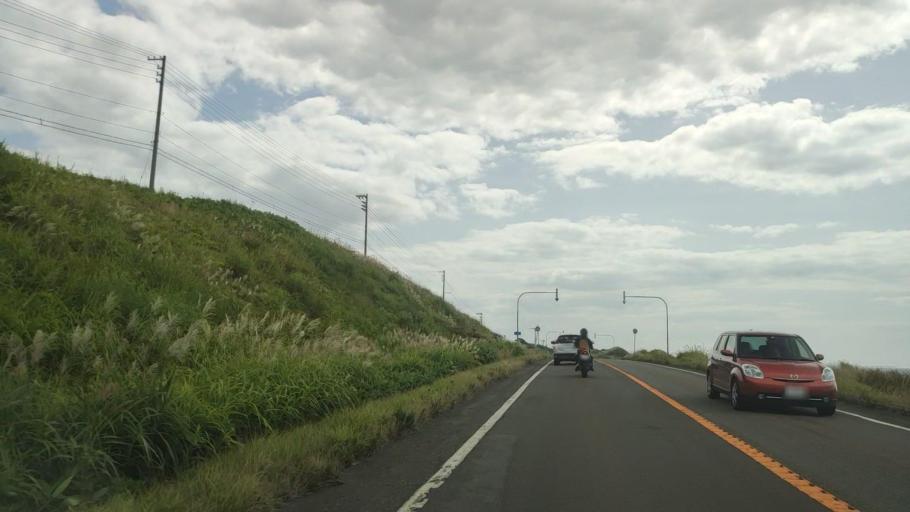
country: JP
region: Hokkaido
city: Rumoi
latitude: 44.5037
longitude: 141.7648
